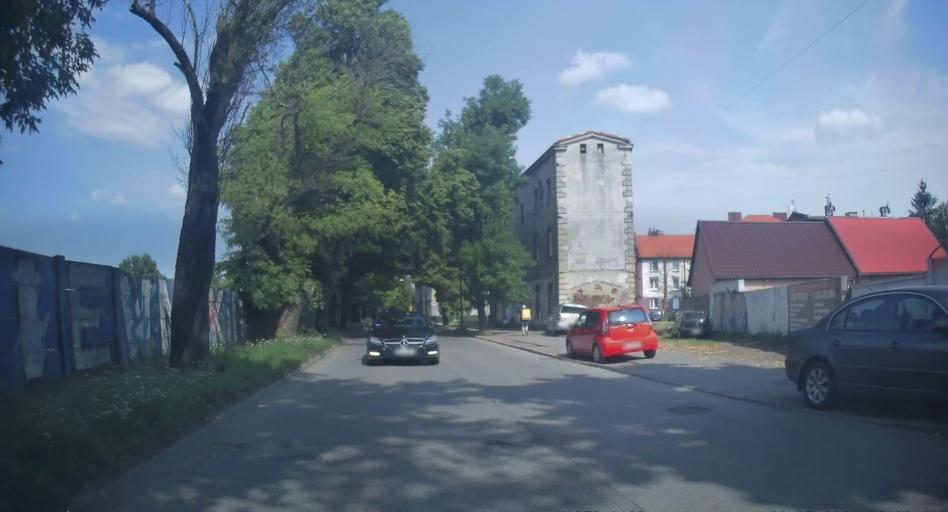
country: PL
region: Silesian Voivodeship
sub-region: Bytom
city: Bytom
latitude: 50.3290
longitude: 18.9336
